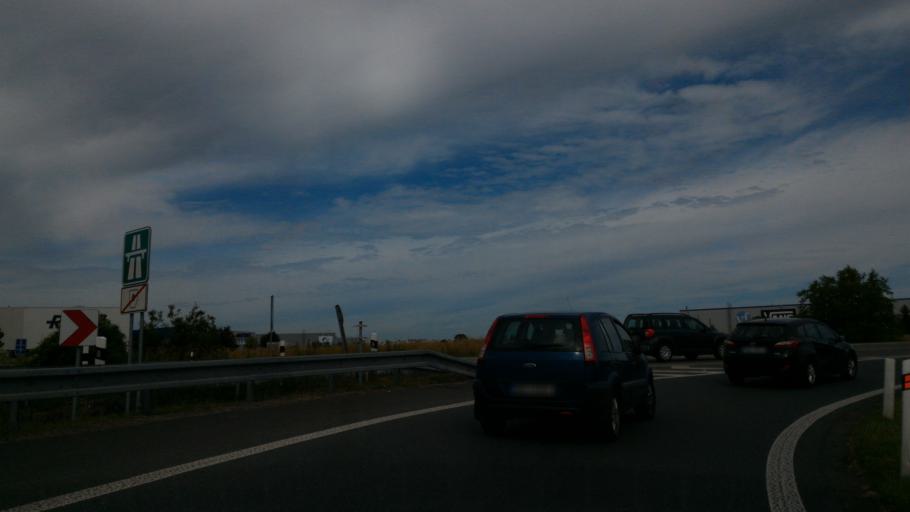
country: CZ
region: Central Bohemia
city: Zdiby
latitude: 50.1748
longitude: 14.4516
